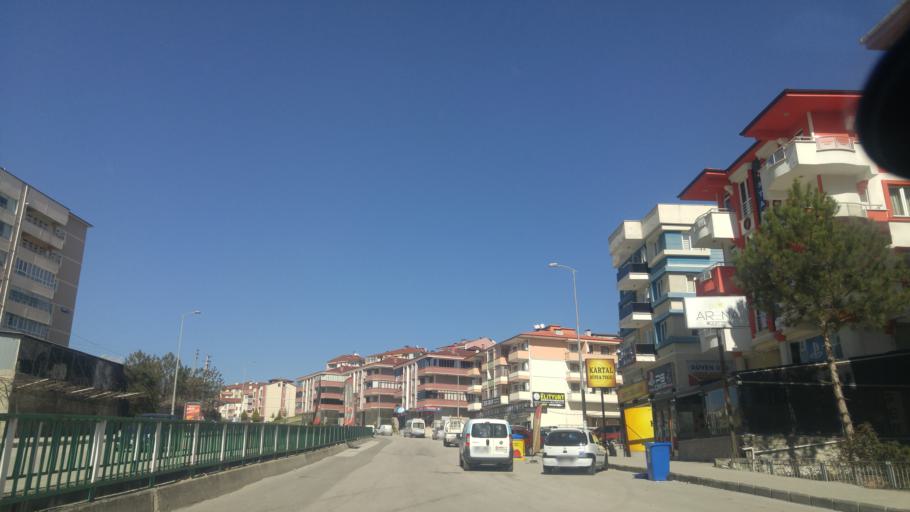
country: TR
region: Karabuk
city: Karabuk
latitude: 41.2217
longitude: 32.6617
